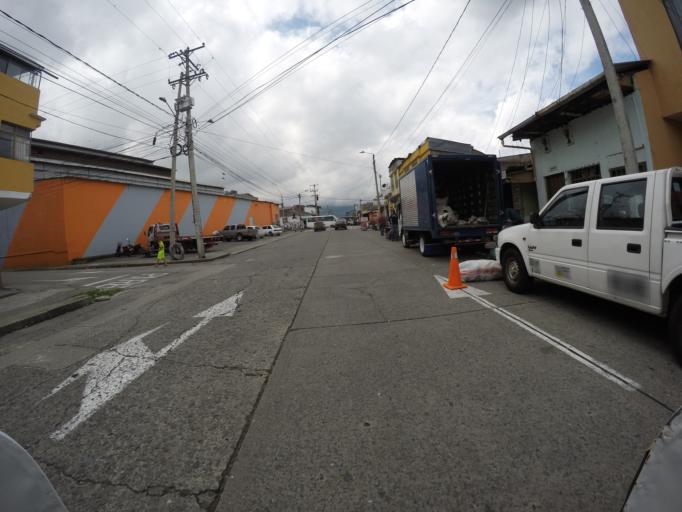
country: CO
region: Quindio
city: Armenia
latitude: 4.5312
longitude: -75.6809
